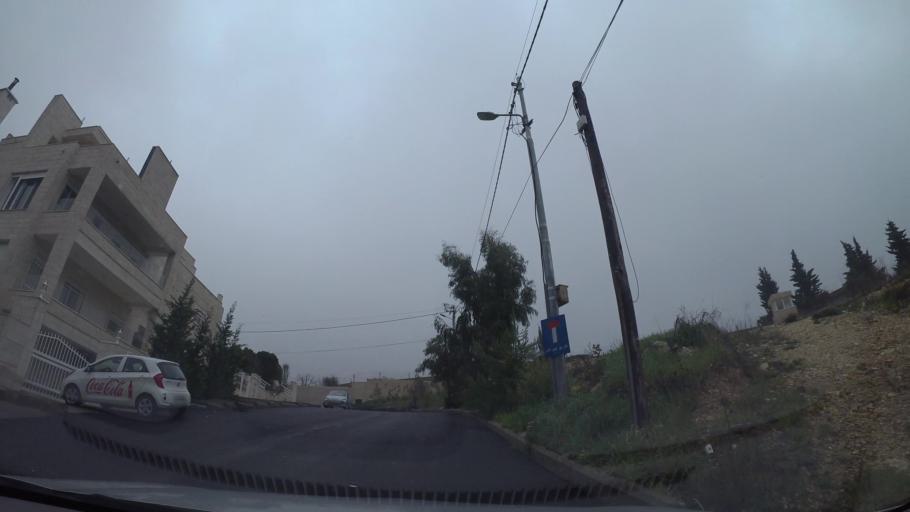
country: JO
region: Amman
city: Wadi as Sir
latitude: 32.0012
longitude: 35.8200
